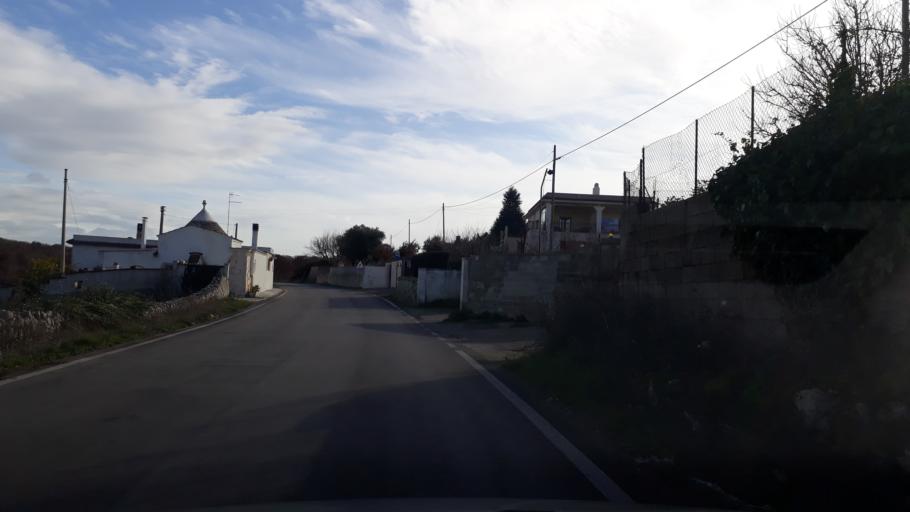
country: IT
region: Apulia
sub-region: Provincia di Taranto
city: Martina Franca
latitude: 40.6784
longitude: 17.3567
